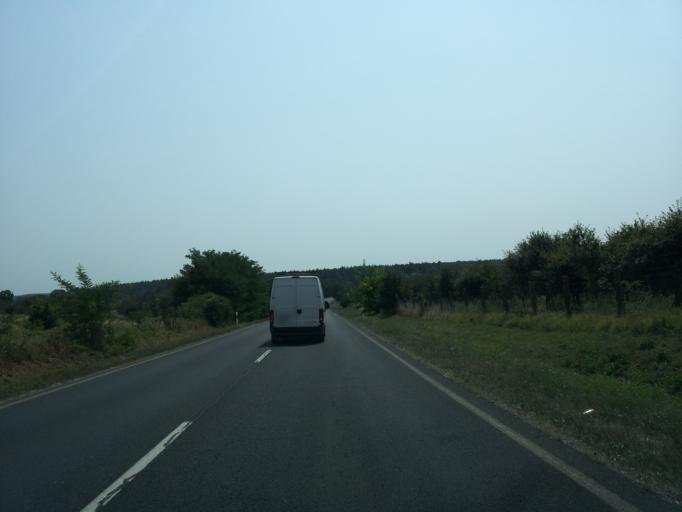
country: HU
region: Veszprem
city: Nemesvamos
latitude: 47.0383
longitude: 17.9145
